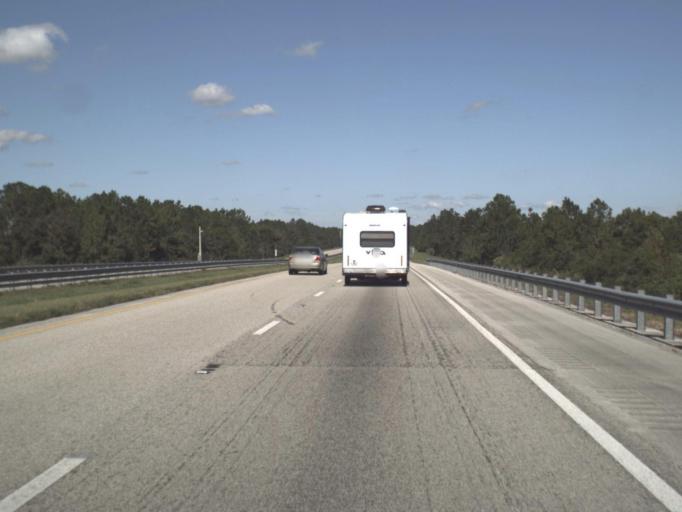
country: US
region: Florida
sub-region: Brevard County
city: June Park
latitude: 27.9107
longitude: -81.0510
